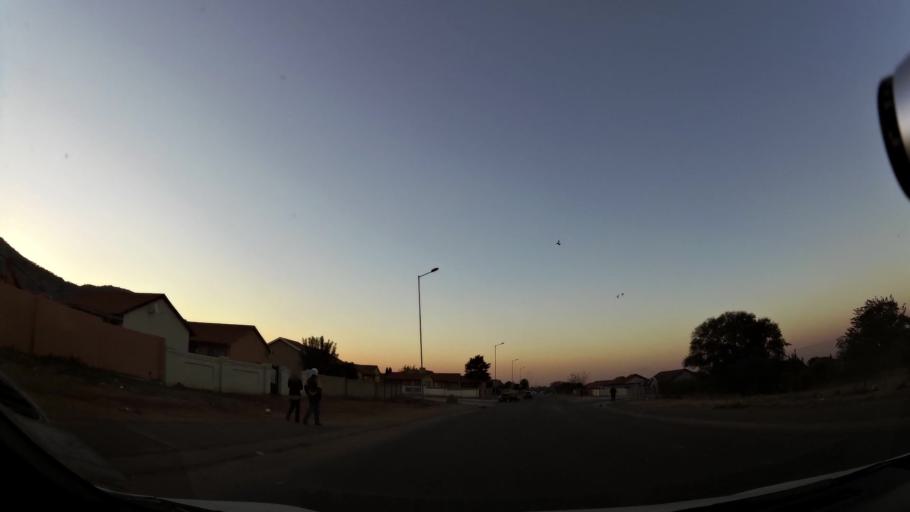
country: ZA
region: North-West
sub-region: Bojanala Platinum District Municipality
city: Rustenburg
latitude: -25.6498
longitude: 27.2009
